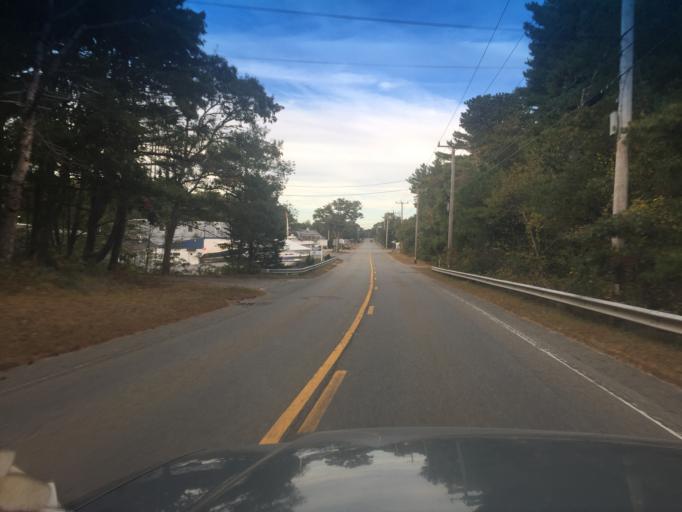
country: US
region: Massachusetts
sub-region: Barnstable County
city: North Falmouth
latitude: 41.6633
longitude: -70.6046
